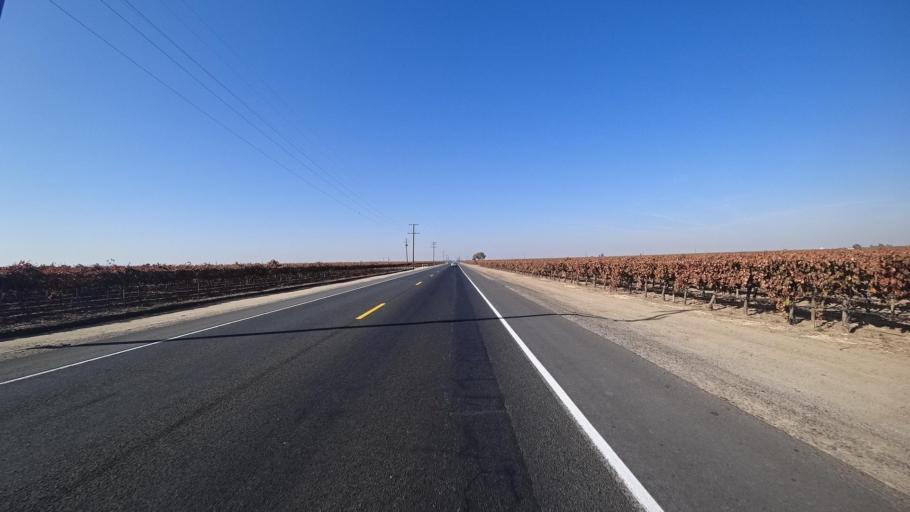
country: US
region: California
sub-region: Kern County
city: Delano
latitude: 35.7178
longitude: -119.2702
